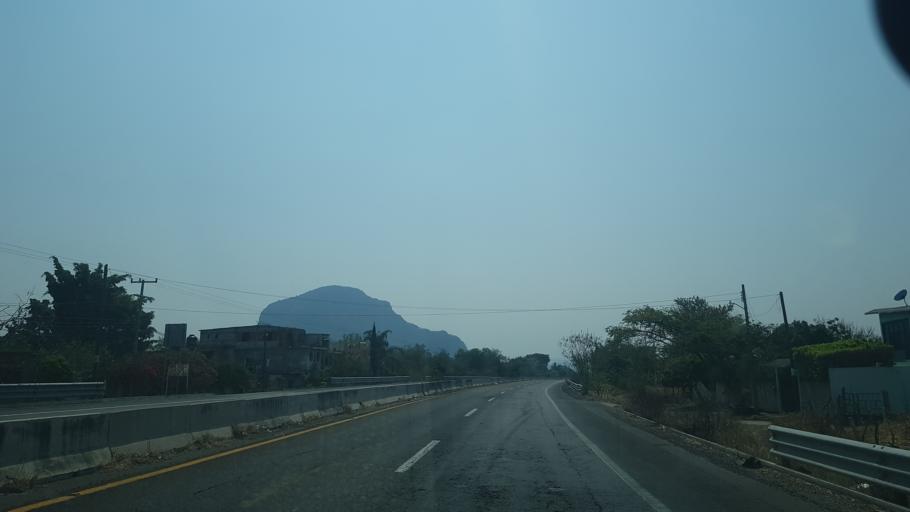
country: MX
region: Morelos
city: Jantetelco
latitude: 18.7135
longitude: -98.7852
